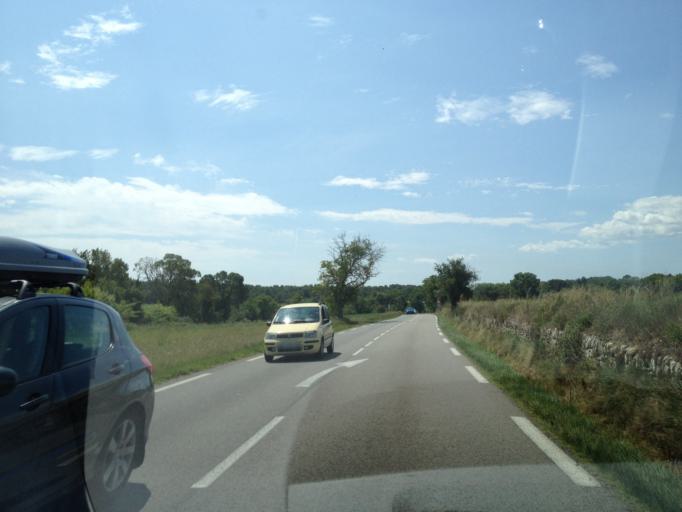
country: FR
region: Languedoc-Roussillon
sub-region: Departement du Gard
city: Villevieille
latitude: 43.8165
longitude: 4.0955
